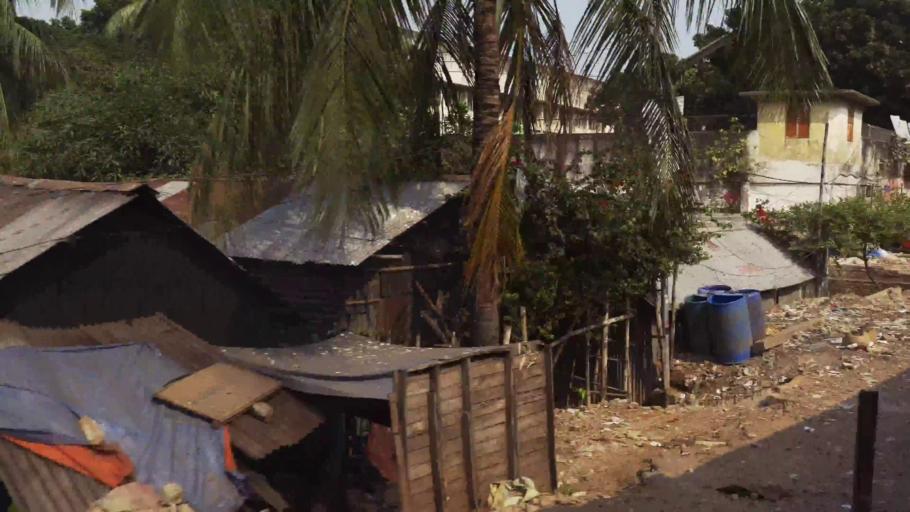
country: BD
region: Dhaka
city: Paltan
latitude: 23.7577
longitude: 90.3945
